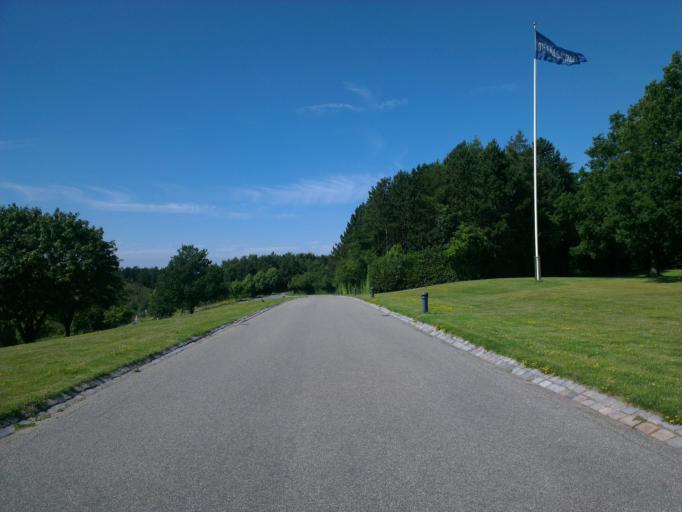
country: DK
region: Capital Region
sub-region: Frederikssund Kommune
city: Slangerup
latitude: 55.8255
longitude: 12.1946
